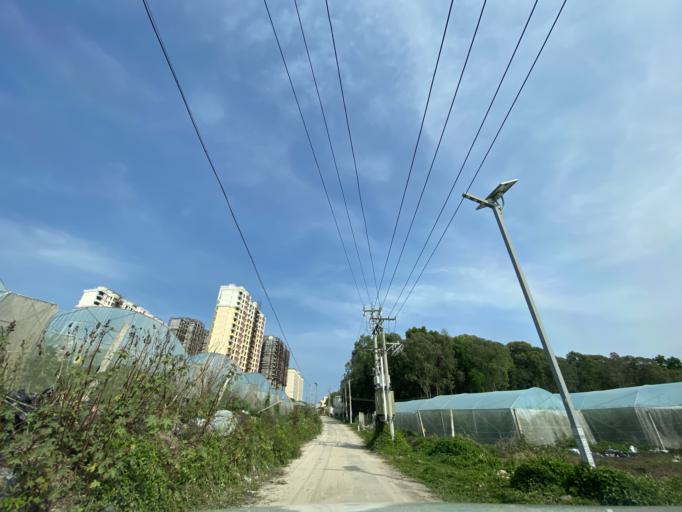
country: CN
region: Hainan
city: Yingzhou
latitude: 18.4047
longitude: 109.8383
